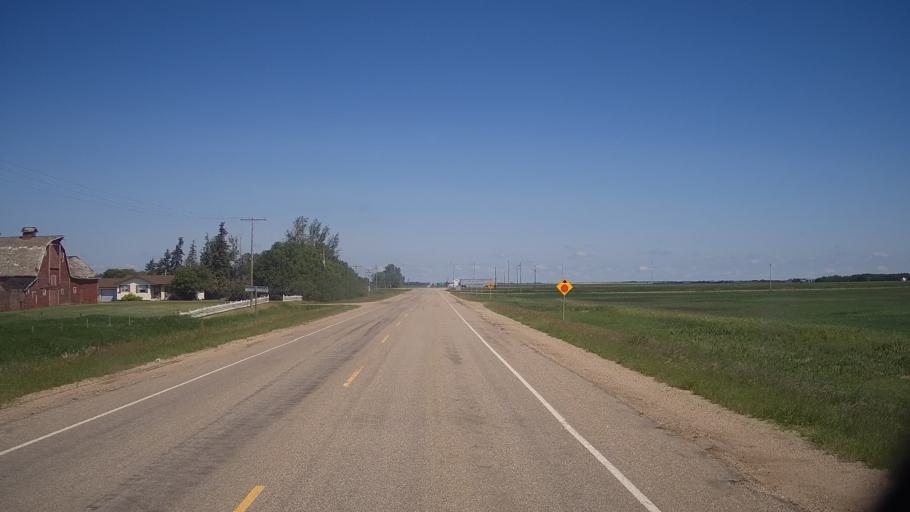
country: CA
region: Saskatchewan
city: Saskatoon
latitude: 51.9880
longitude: -106.0754
